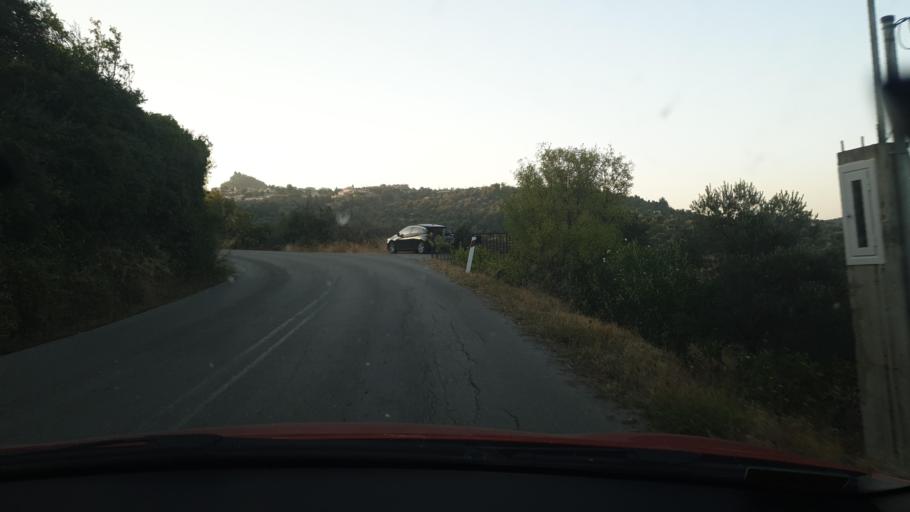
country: GR
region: Central Greece
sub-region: Nomos Evvoias
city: Oxilithos
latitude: 38.5720
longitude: 24.1206
